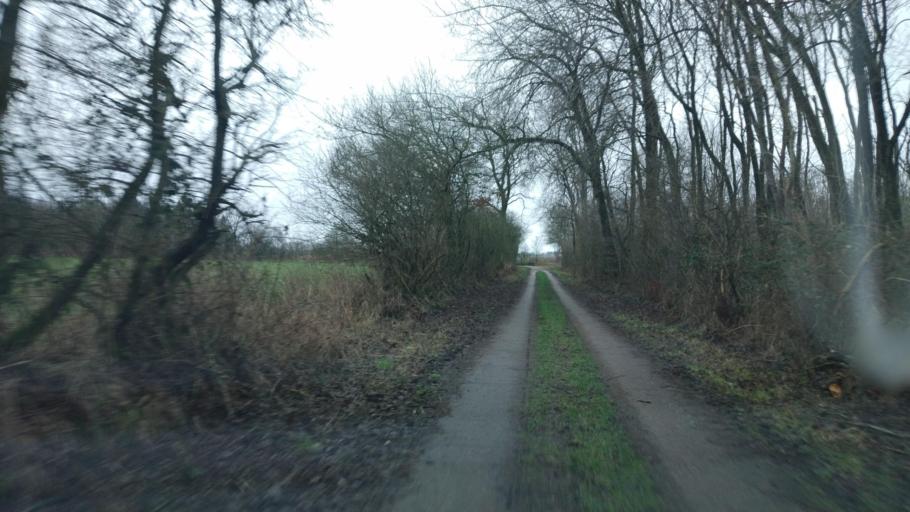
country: DE
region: Schleswig-Holstein
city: Gross Rheide
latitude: 54.4612
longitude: 9.4310
